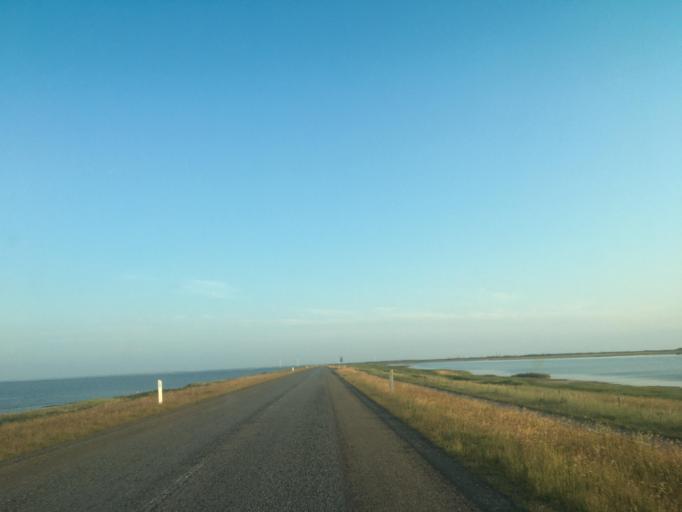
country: DK
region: Central Jutland
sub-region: Lemvig Kommune
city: Thyboron
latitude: 56.7464
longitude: 8.2508
